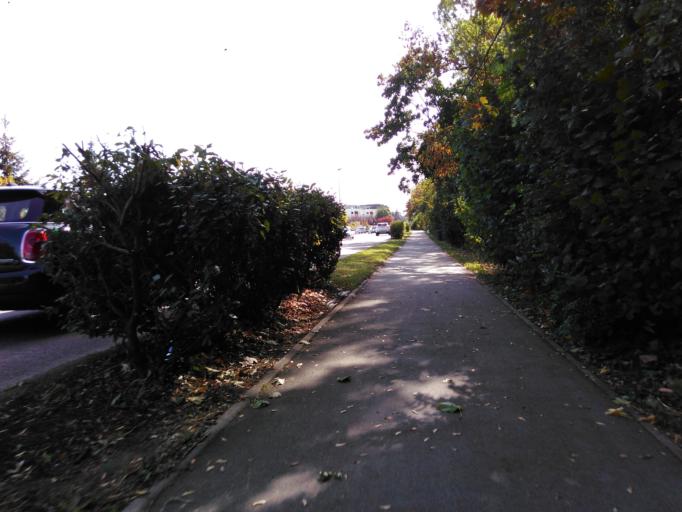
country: FR
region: Lorraine
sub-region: Departement de la Moselle
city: Thionville
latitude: 49.3802
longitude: 6.1693
